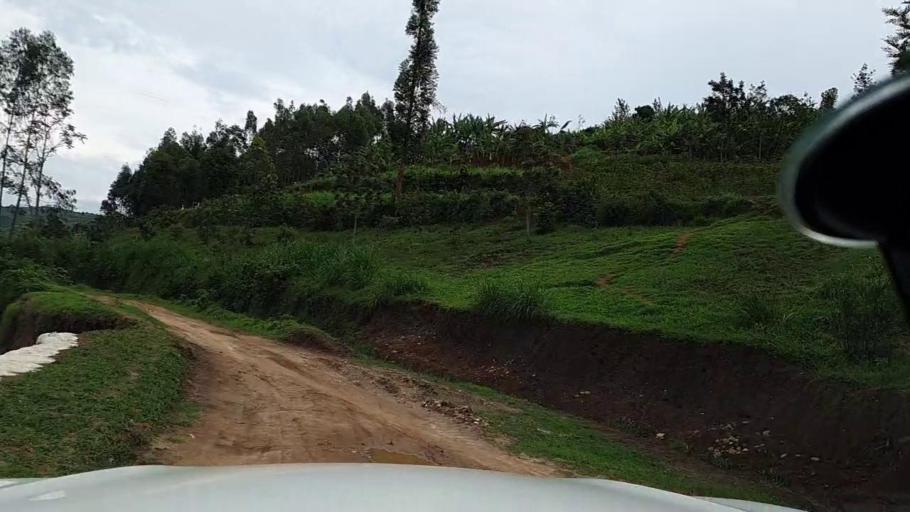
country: RW
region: Southern Province
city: Gitarama
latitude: -2.0959
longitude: 29.6400
